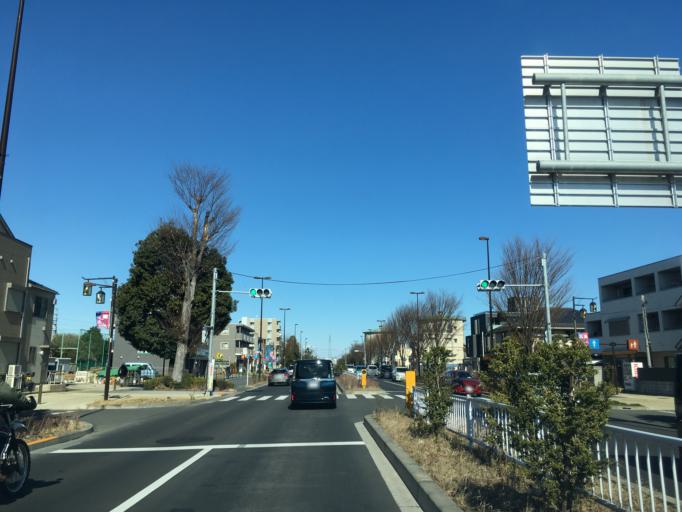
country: JP
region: Tokyo
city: Mitaka-shi
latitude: 35.6845
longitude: 139.5497
